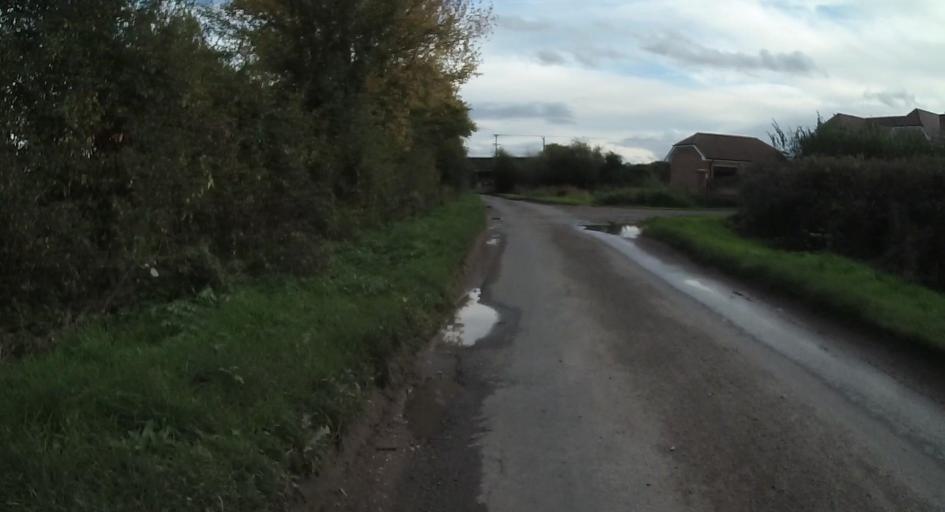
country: GB
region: England
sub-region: Wokingham
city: Swallowfield
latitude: 51.3710
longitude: -0.9591
